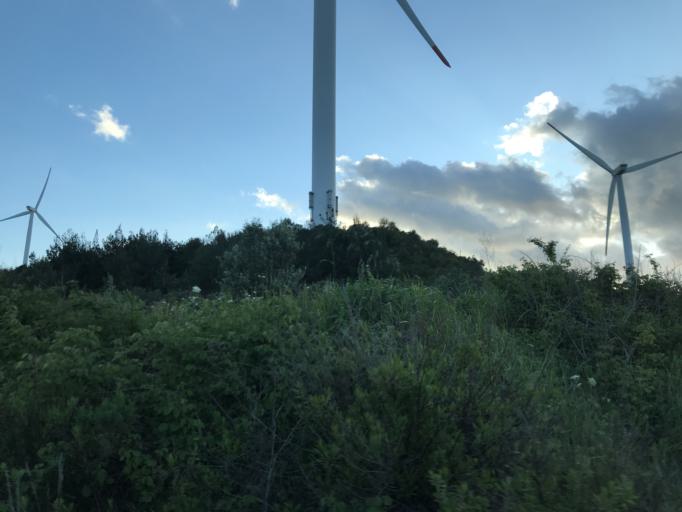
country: TR
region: Hatay
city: Buyukcat
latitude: 36.1059
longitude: 36.0444
